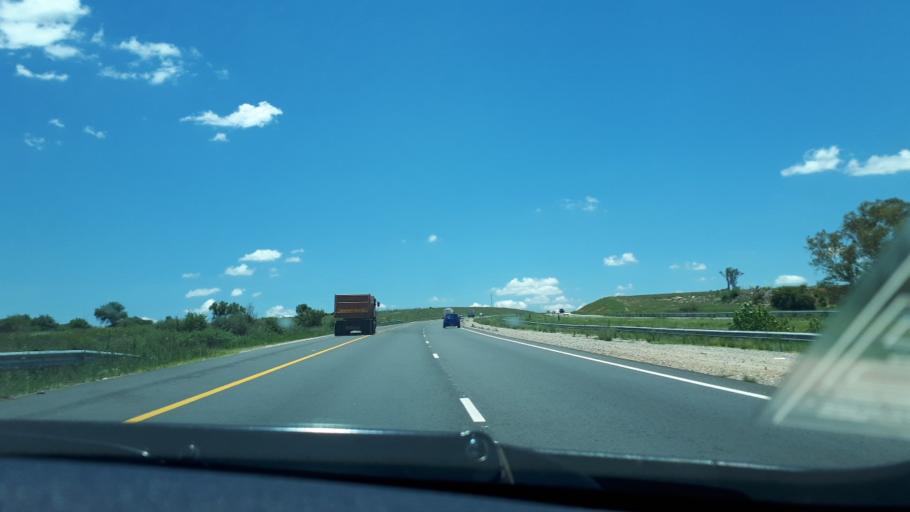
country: ZA
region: Gauteng
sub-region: City of Johannesburg Metropolitan Municipality
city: Diepsloot
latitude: -25.9438
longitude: 27.9610
